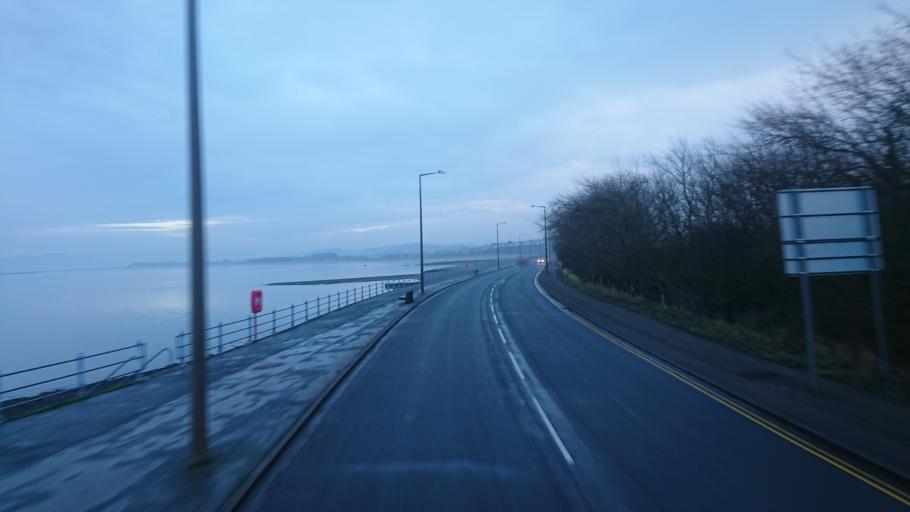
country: GB
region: England
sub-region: Lancashire
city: Morecambe
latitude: 54.0846
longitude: -2.8318
